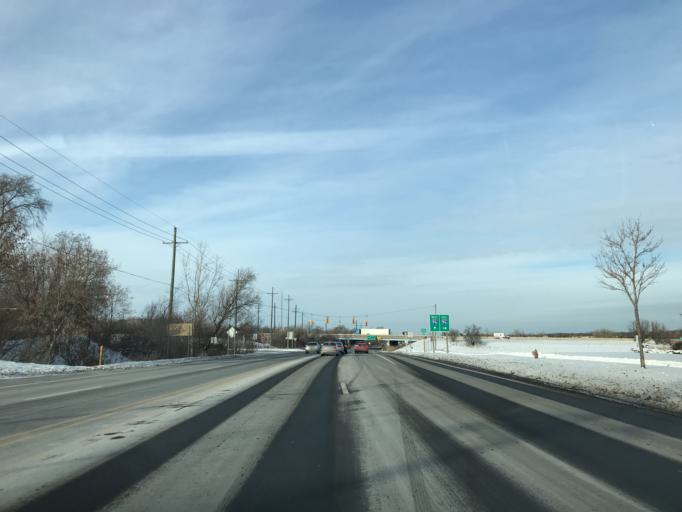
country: US
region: Michigan
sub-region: Oakland County
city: South Lyon
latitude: 42.5161
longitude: -83.6161
